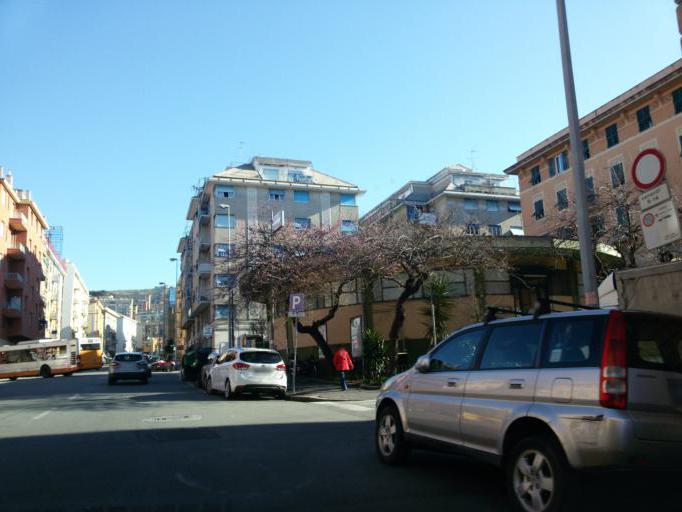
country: IT
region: Liguria
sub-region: Provincia di Genova
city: Genoa
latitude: 44.3997
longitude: 8.9817
